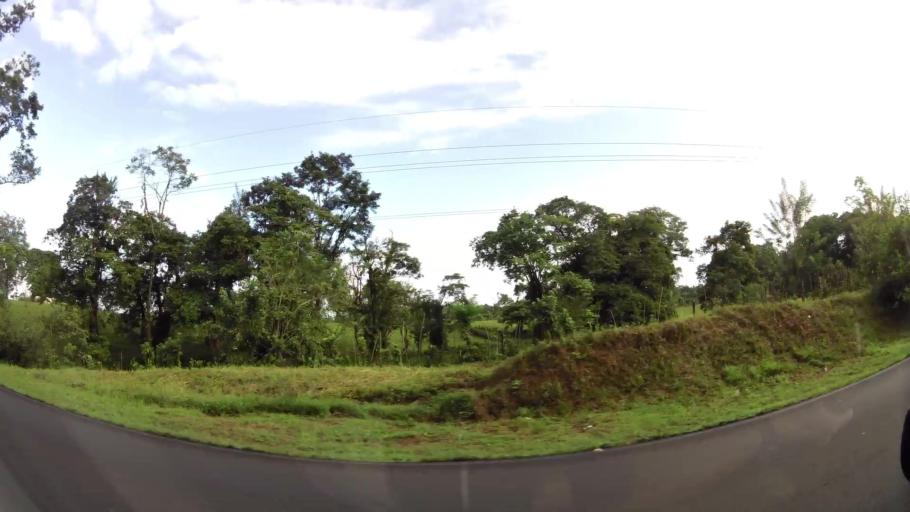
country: CR
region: Limon
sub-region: Canton de Guacimo
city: Guacimo
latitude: 10.1973
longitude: -83.6555
